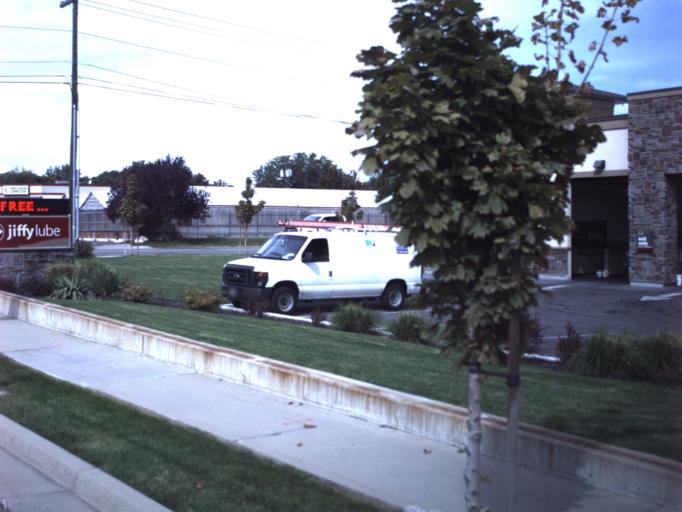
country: US
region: Utah
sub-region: Salt Lake County
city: Taylorsville
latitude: 40.6532
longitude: -111.9478
